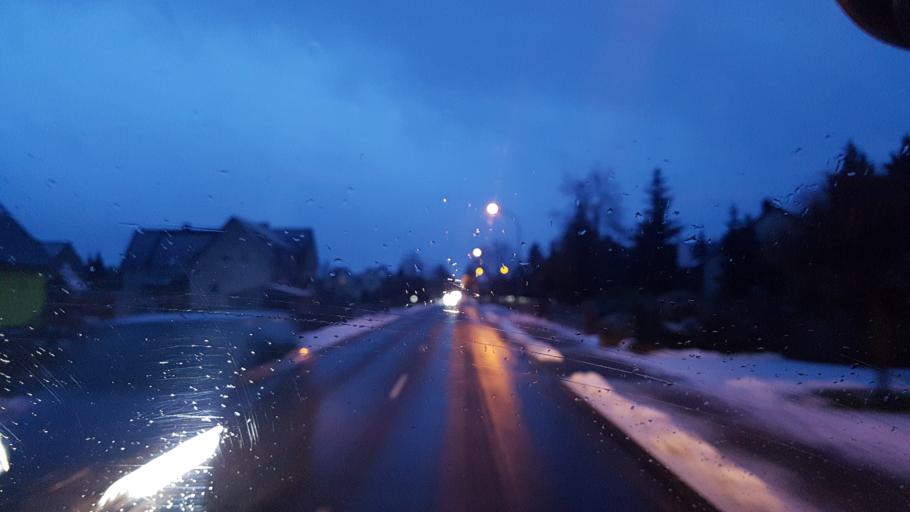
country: DE
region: Brandenburg
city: Briesen
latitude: 51.8128
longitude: 14.2453
